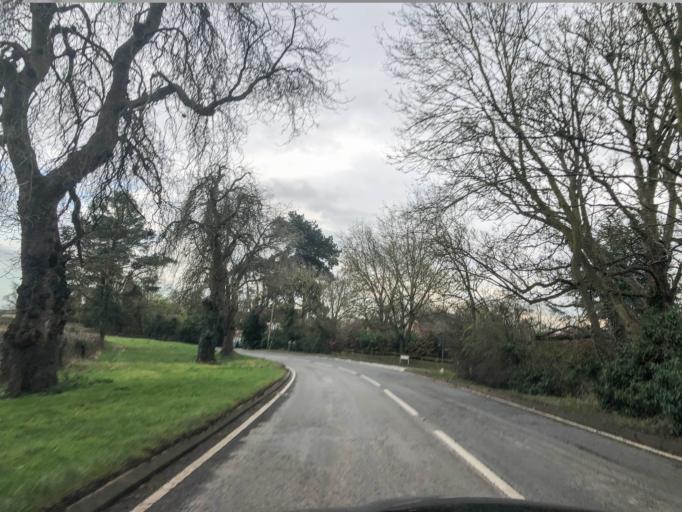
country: GB
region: England
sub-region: Warwickshire
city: Wroxall
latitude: 52.3053
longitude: -1.6828
